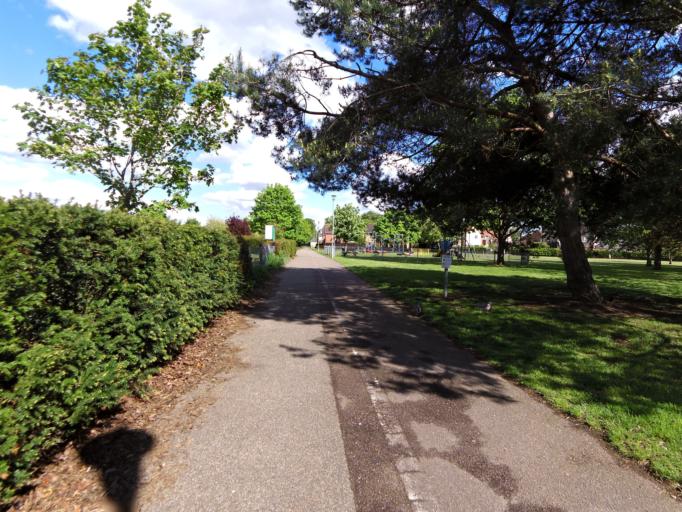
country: GB
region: England
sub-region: Suffolk
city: Thurston
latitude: 52.2509
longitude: 0.8121
